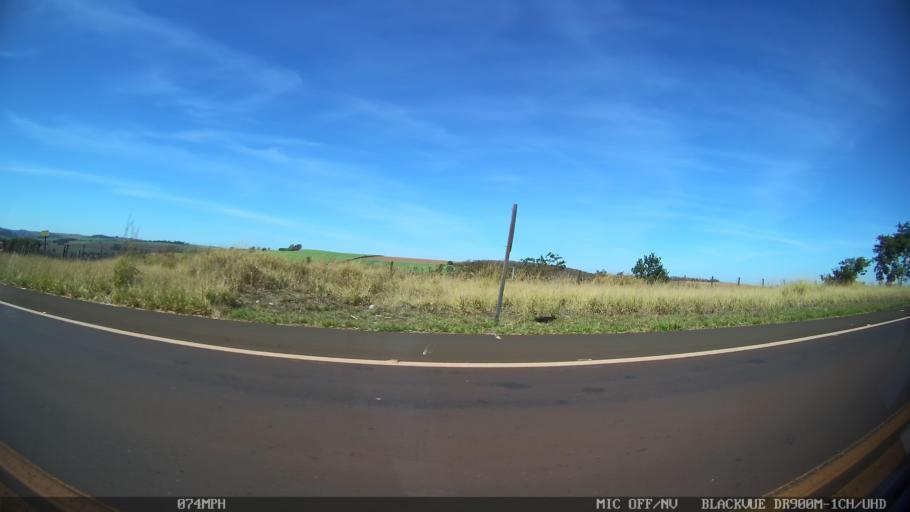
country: BR
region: Sao Paulo
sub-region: Sao Joaquim Da Barra
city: Sao Joaquim da Barra
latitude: -20.5601
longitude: -47.6839
